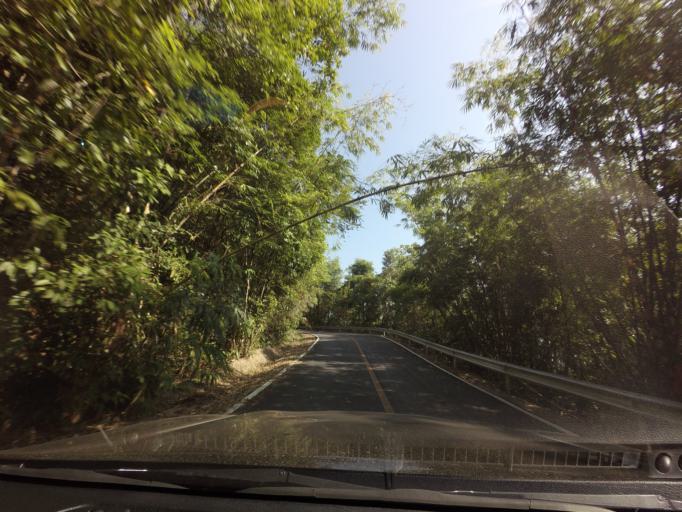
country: TH
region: Kanchanaburi
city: Thong Pha Phum
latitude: 14.6876
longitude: 98.4046
